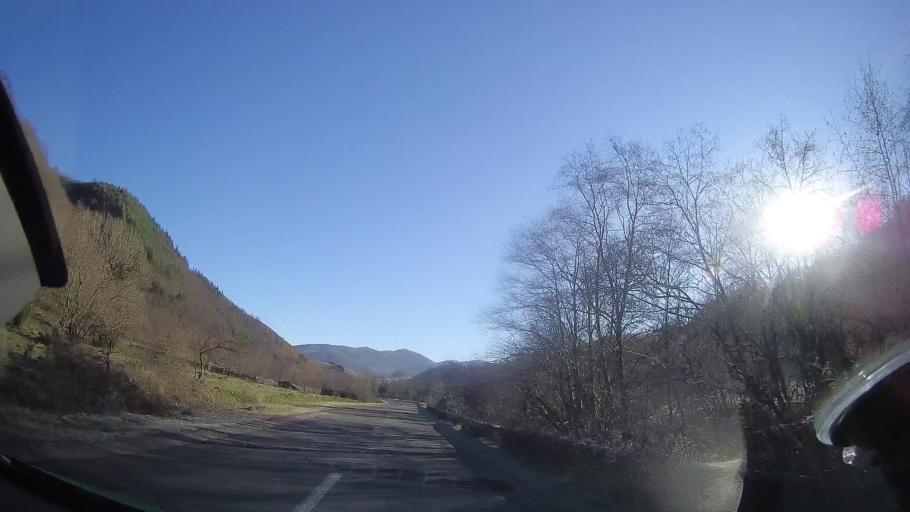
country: RO
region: Cluj
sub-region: Comuna Sacueu
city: Sacuieu
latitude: 46.8312
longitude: 22.8689
